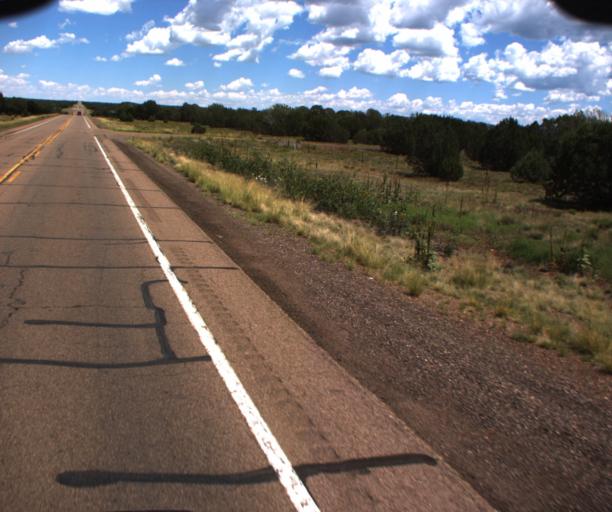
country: US
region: Arizona
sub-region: Navajo County
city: Show Low
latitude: 34.2671
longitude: -109.9447
